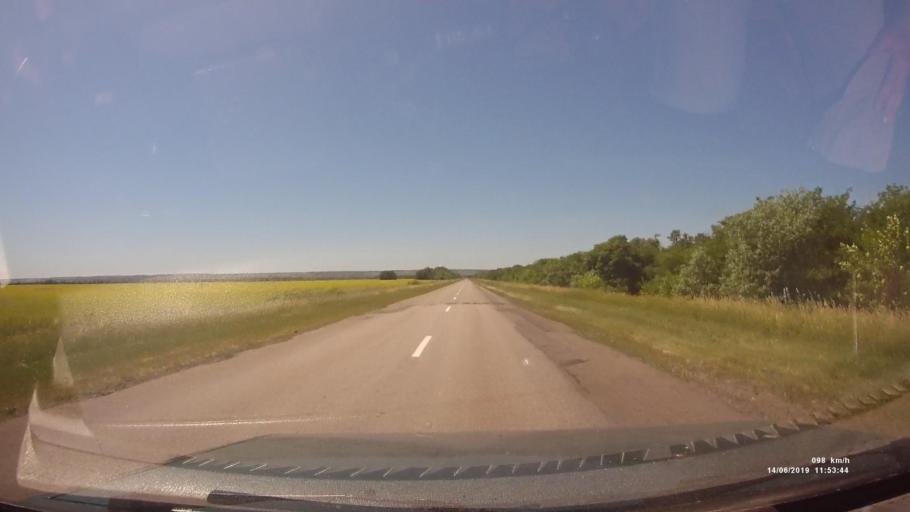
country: RU
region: Rostov
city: Kazanskaya
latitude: 49.8248
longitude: 41.2068
